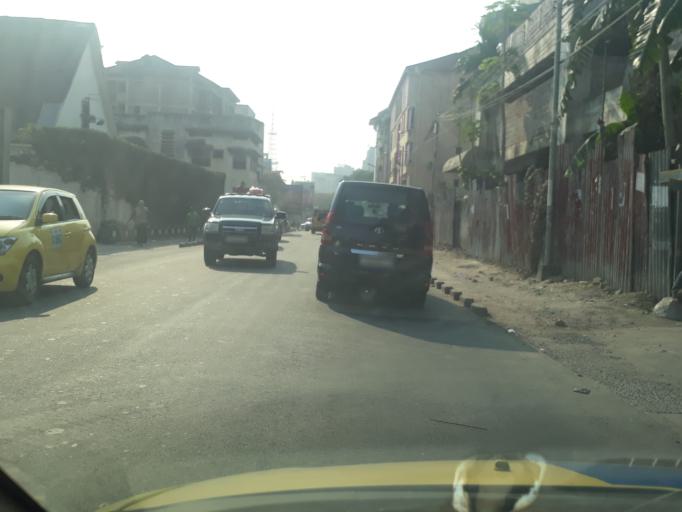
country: CD
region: Kinshasa
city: Kinshasa
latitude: -4.3058
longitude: 15.3225
